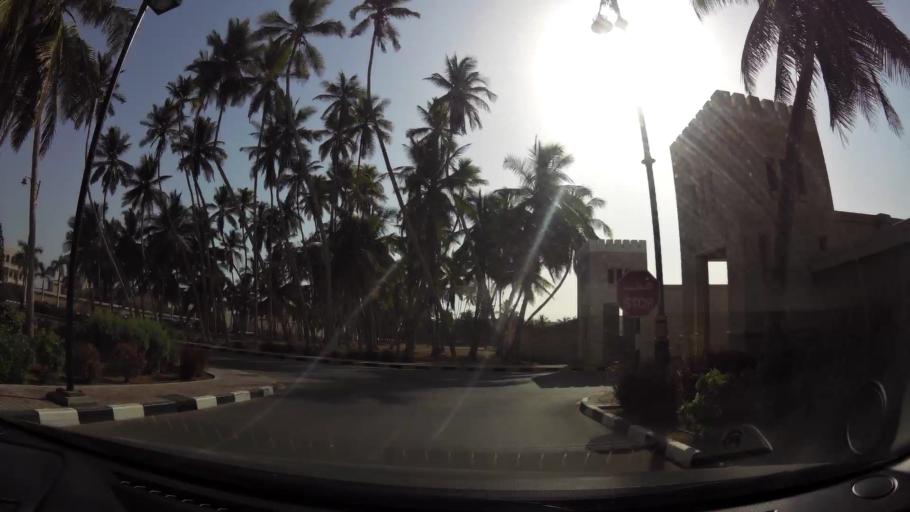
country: OM
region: Zufar
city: Salalah
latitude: 17.0007
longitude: 54.0994
